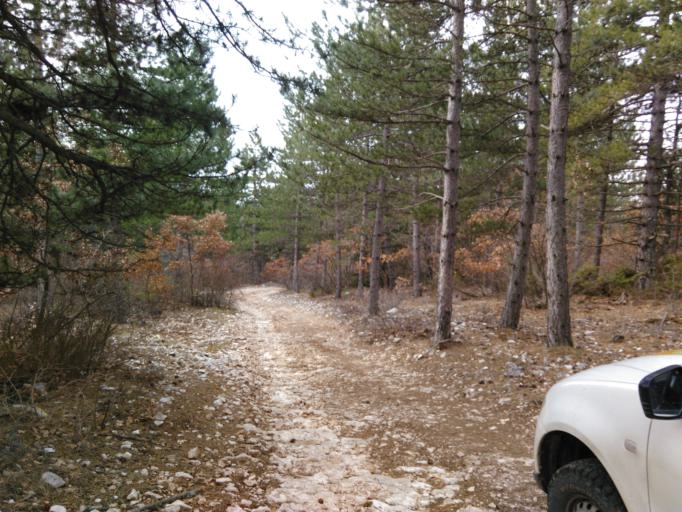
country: FR
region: Provence-Alpes-Cote d'Azur
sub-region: Departement du Vaucluse
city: Villes-sur-Auzon
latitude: 44.1100
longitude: 5.3049
